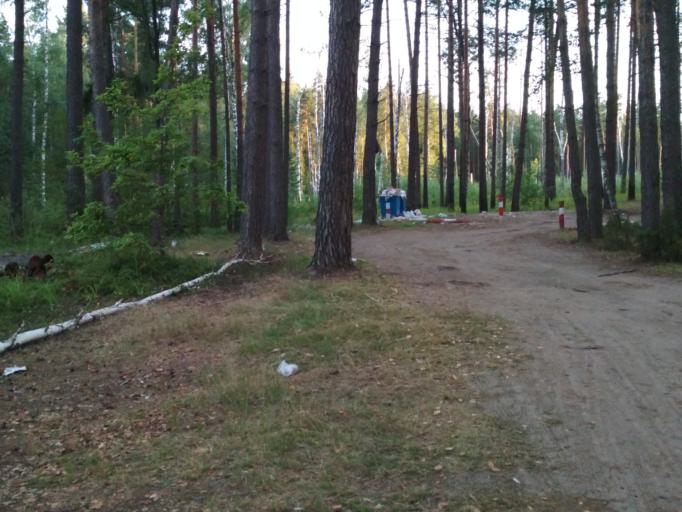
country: RU
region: Rjazan
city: Solotcha
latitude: 54.8258
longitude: 39.9563
